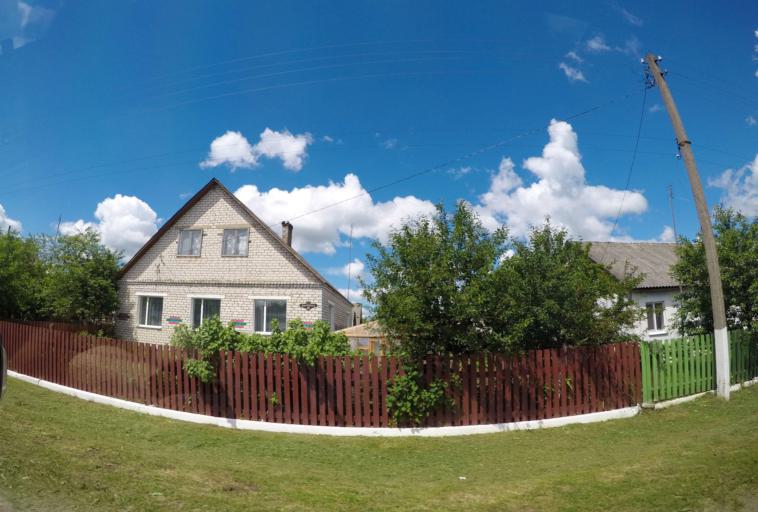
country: BY
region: Grodnenskaya
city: Hal'shany
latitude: 54.1666
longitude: 26.0935
